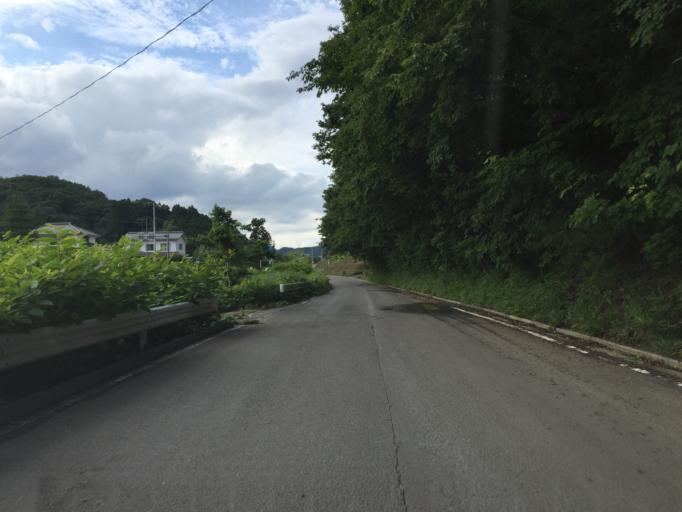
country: JP
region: Fukushima
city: Fukushima-shi
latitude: 37.7003
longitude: 140.5089
